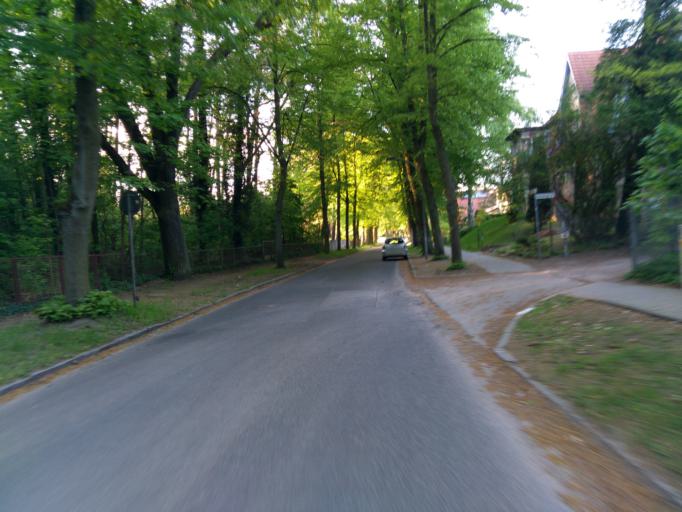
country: DE
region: Brandenburg
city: Falkensee
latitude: 52.5762
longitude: 13.0940
